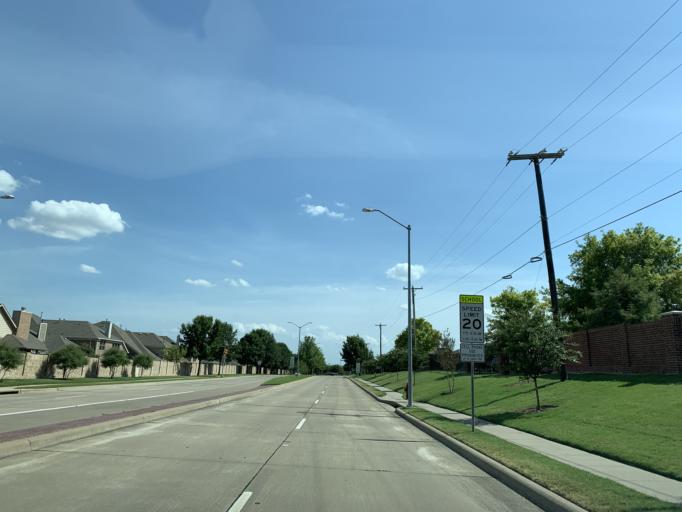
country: US
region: Texas
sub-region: Dallas County
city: Cedar Hill
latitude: 32.6498
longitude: -97.0072
